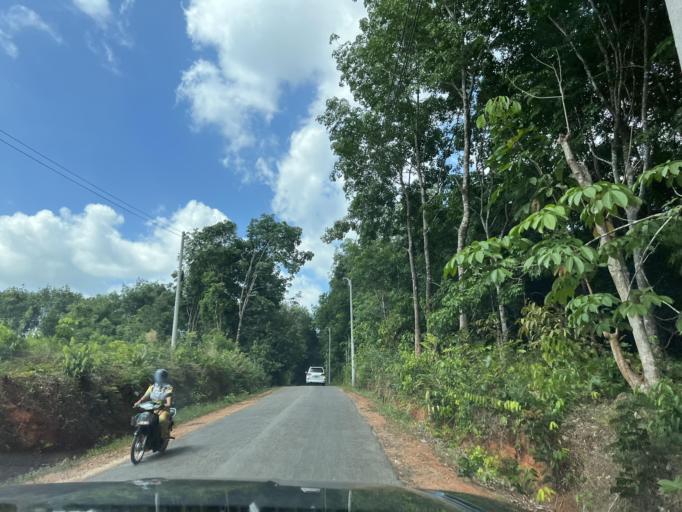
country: MM
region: Tanintharyi
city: Dawei
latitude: 14.6206
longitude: 97.9493
